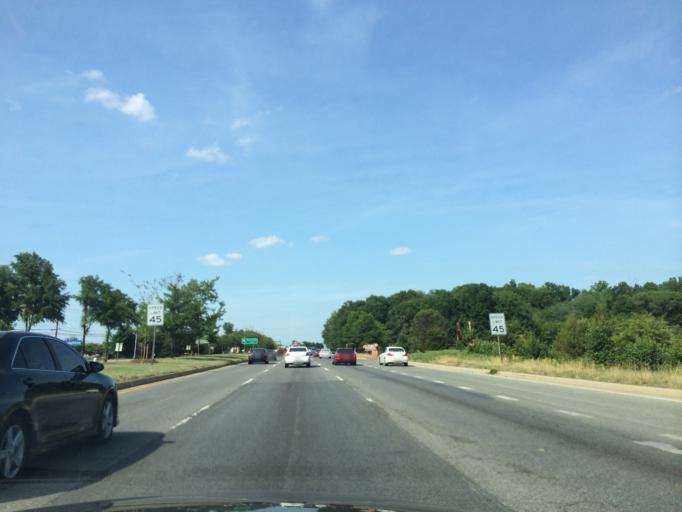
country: US
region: Maryland
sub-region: Charles County
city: Waldorf
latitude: 38.6401
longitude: -76.8965
